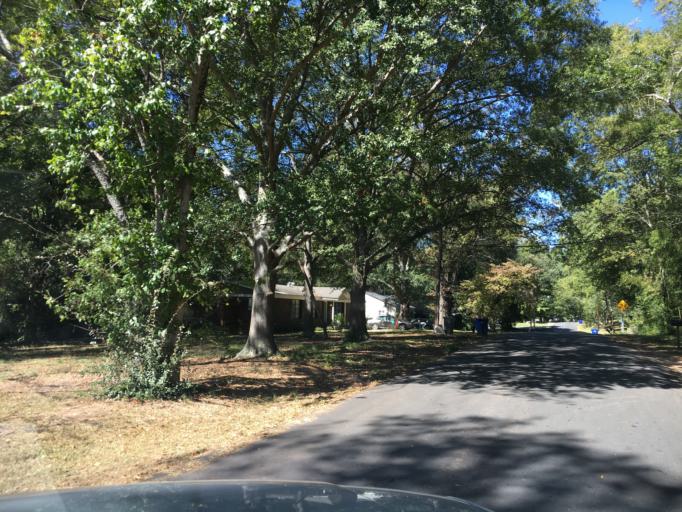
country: US
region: South Carolina
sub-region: Spartanburg County
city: Spartanburg
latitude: 34.9305
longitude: -81.9014
